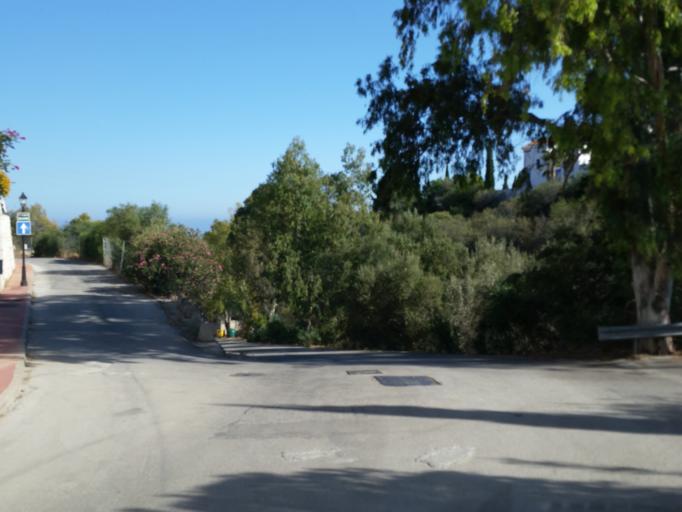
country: ES
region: Andalusia
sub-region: Provincia de Malaga
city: Mijas
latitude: 36.5774
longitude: -4.6073
